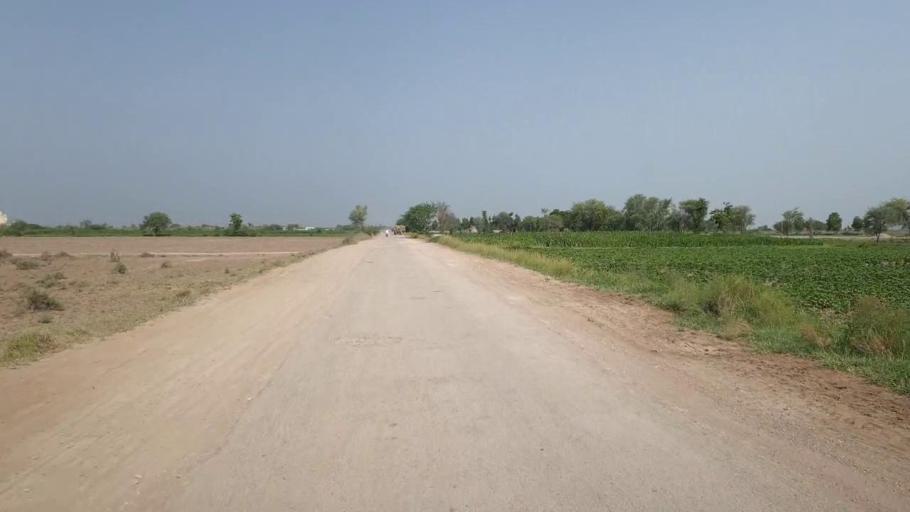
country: PK
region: Sindh
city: Daulatpur
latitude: 26.5501
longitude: 68.0578
